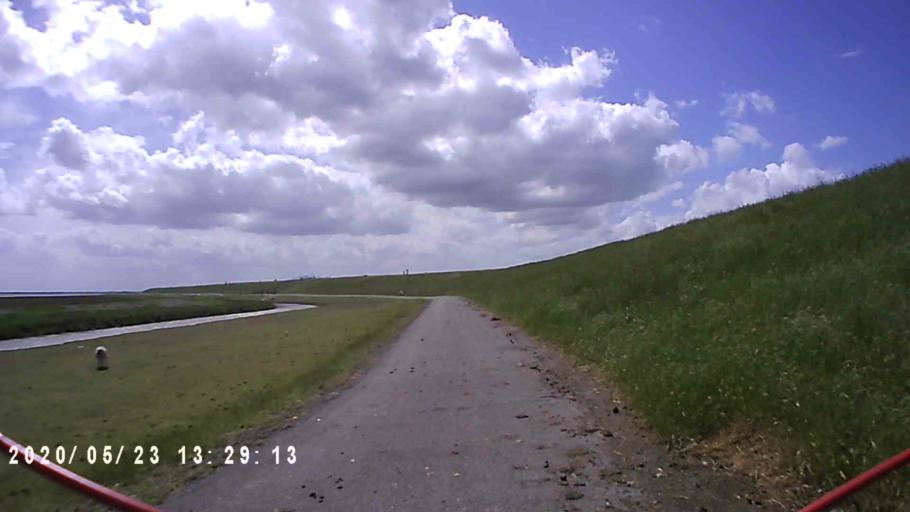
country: NL
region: Groningen
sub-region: Gemeente  Oldambt
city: Winschoten
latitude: 53.2792
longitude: 7.0813
